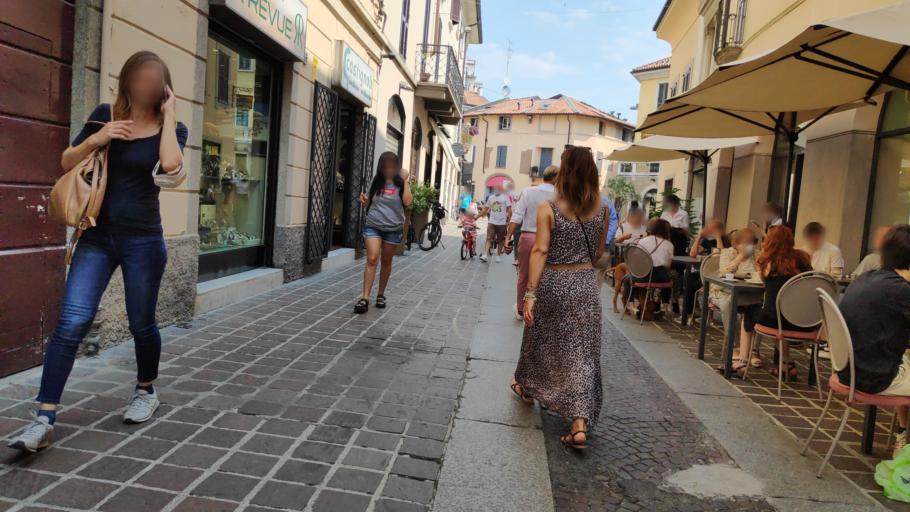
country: IT
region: Lombardy
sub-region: Provincia di Monza e Brianza
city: Monza
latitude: 45.5868
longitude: 9.2759
